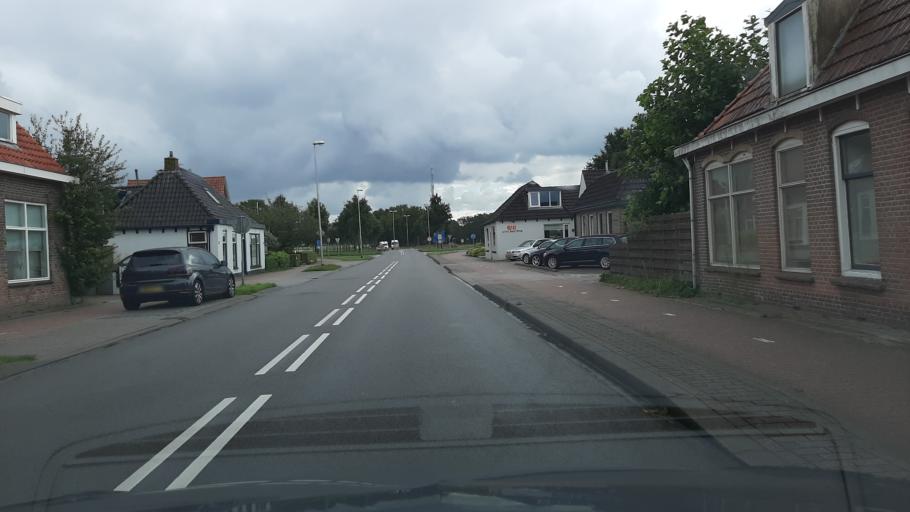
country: NL
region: Overijssel
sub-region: Gemeente Steenwijkerland
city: Tuk
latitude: 52.8070
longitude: 6.0808
